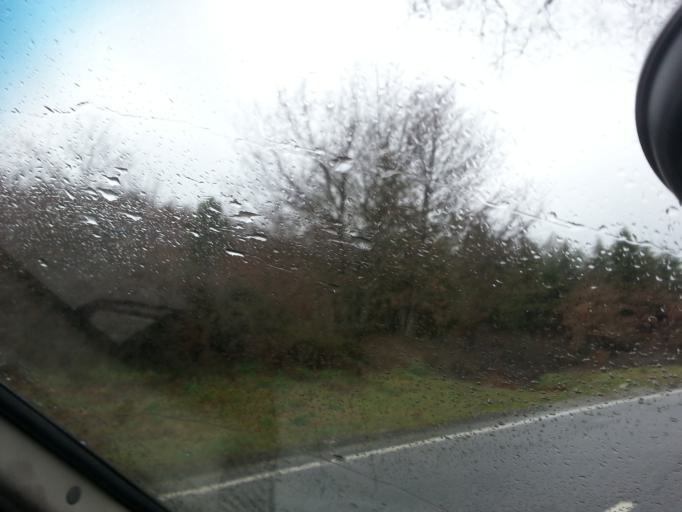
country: PT
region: Viseu
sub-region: Viseu
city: Rio de Loba
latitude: 40.6396
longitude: -7.8405
